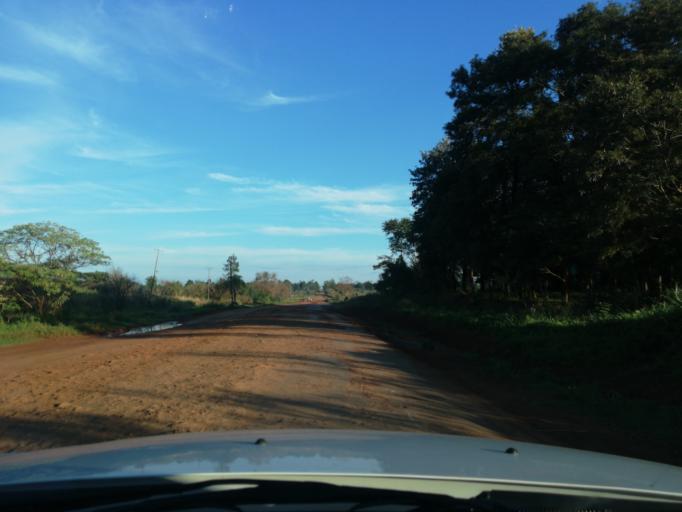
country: AR
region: Misiones
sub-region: Departamento de Capital
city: Posadas
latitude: -27.4670
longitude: -55.9709
